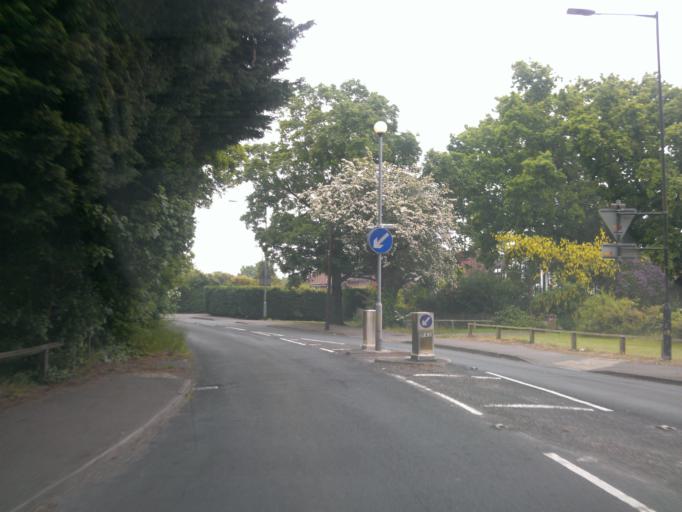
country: GB
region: England
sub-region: Essex
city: West Bergholt
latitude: 51.9066
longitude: 0.8754
